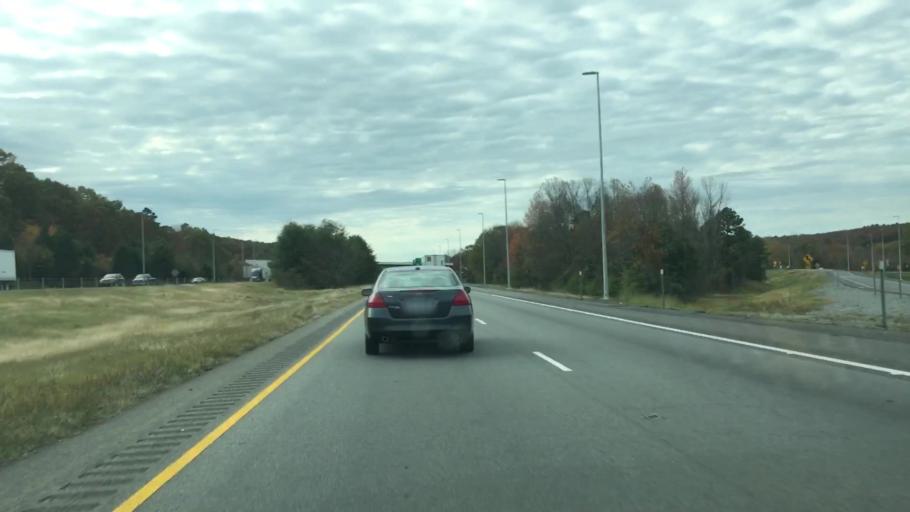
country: US
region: Arkansas
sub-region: Faulkner County
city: Conway
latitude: 35.1189
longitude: -92.4554
